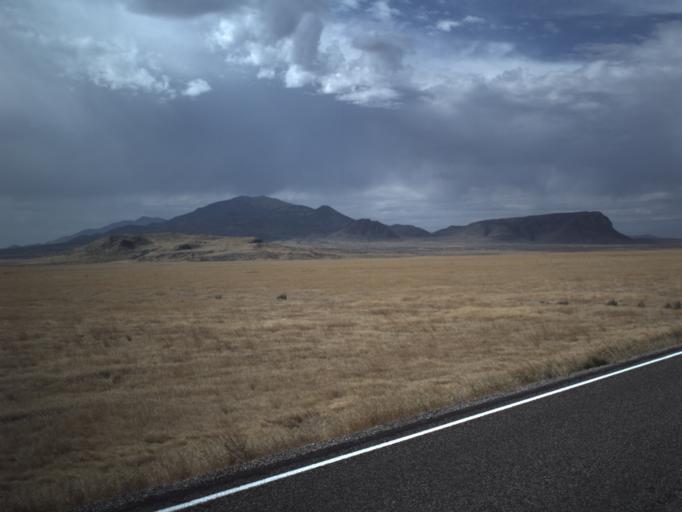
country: US
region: Utah
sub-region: Tooele County
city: Wendover
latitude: 41.3950
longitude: -113.9634
